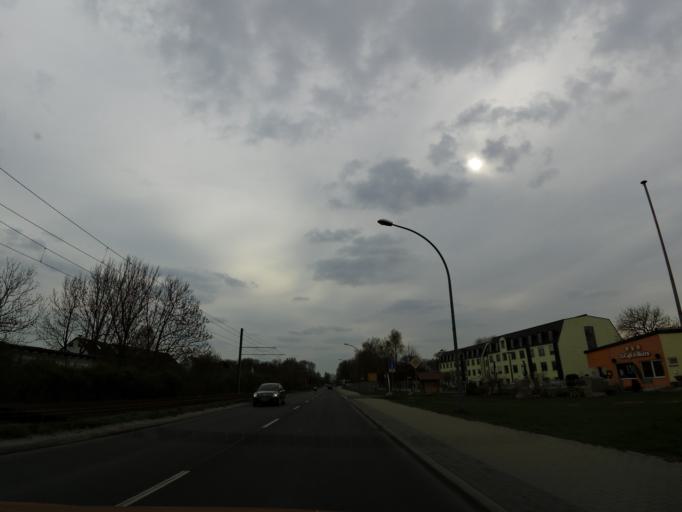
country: DE
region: Brandenburg
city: Mullrose
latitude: 52.2972
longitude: 14.4722
